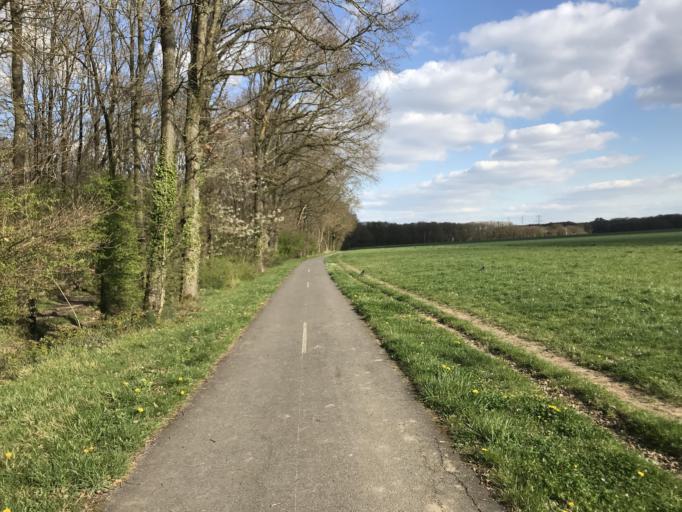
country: FR
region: Ile-de-France
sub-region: Departement de l'Essonne
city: Vauhallan
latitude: 48.7481
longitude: 2.2027
